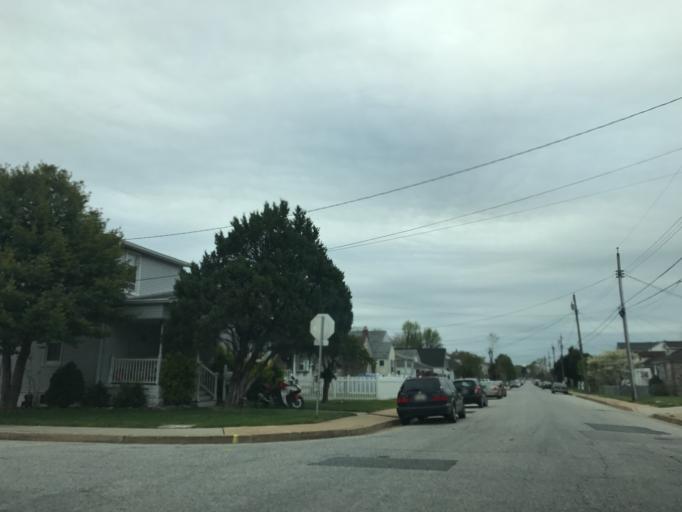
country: US
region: Maryland
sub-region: Baltimore County
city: Essex
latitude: 39.3065
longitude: -76.4752
